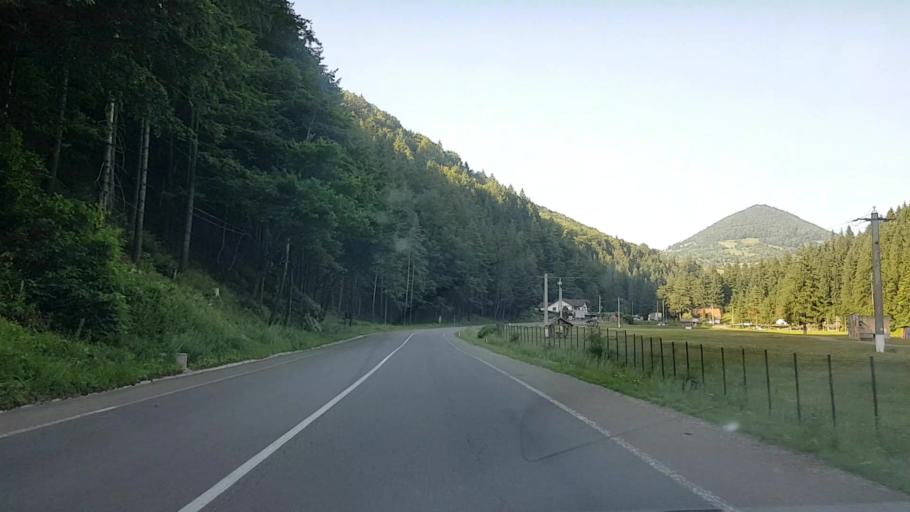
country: RO
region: Bistrita-Nasaud
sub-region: Comuna Tiha Bargaului
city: Tureac
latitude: 47.2161
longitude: 24.8920
